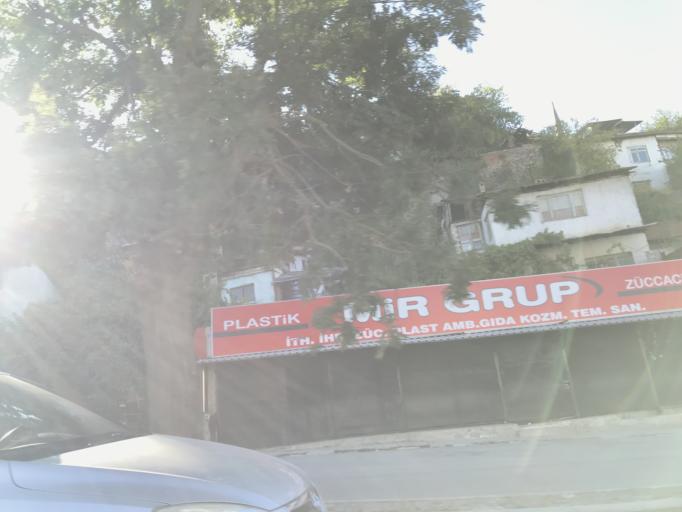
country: TR
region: Ankara
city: Cankaya
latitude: 39.9394
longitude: 32.8716
